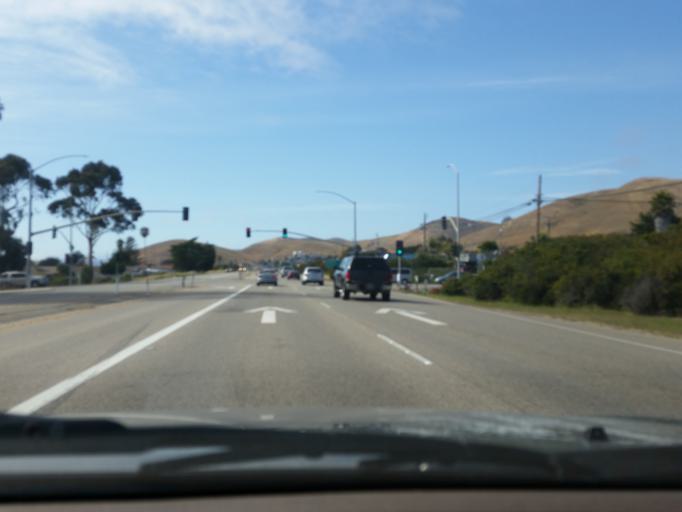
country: US
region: California
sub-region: San Luis Obispo County
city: Morro Bay
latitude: 35.3931
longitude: -120.8602
